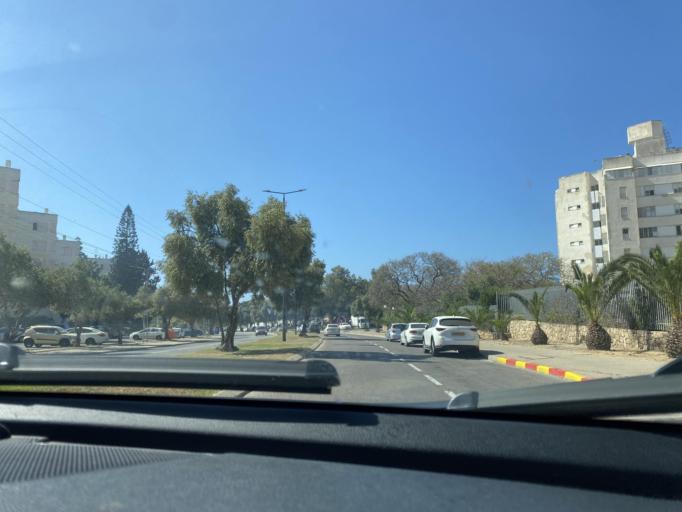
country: IL
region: Southern District
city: Ashqelon
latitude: 31.6825
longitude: 34.5700
